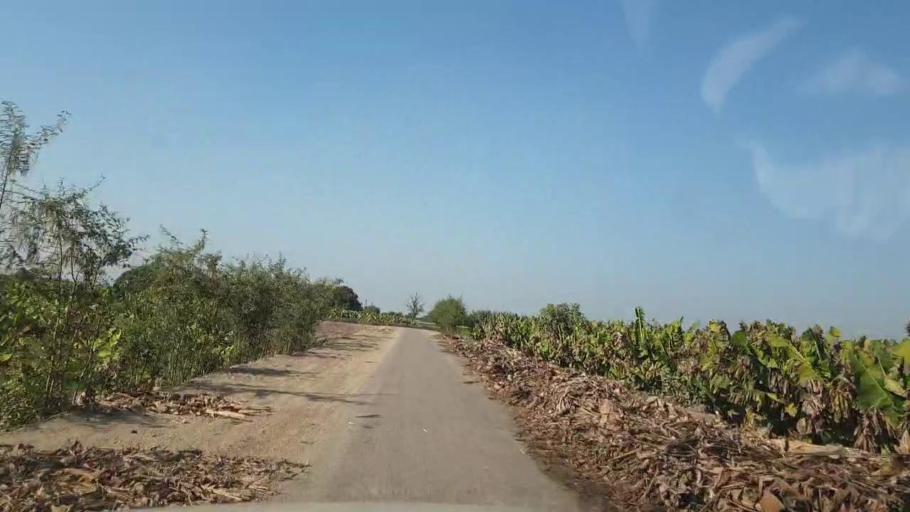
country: PK
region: Sindh
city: Tando Allahyar
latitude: 25.4798
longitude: 68.6600
